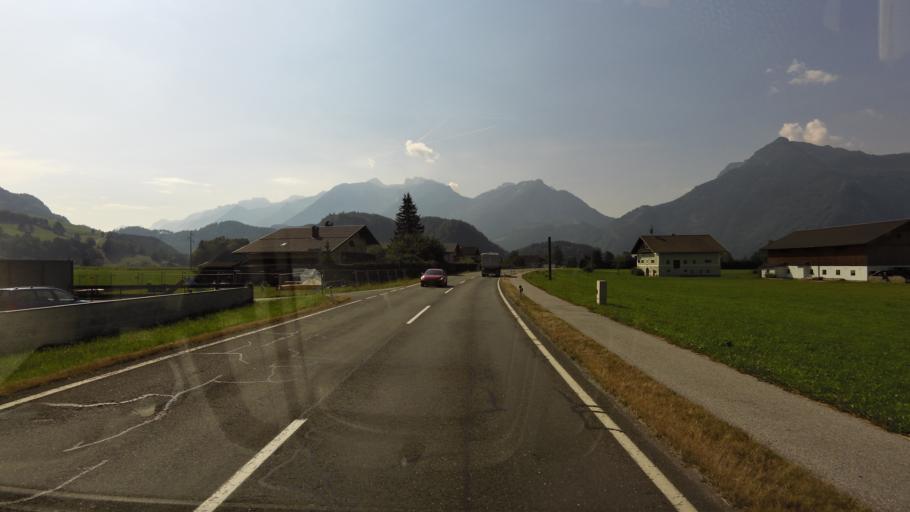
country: AT
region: Salzburg
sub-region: Politischer Bezirk Hallein
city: Golling an der Salzach
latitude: 47.6127
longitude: 13.1668
